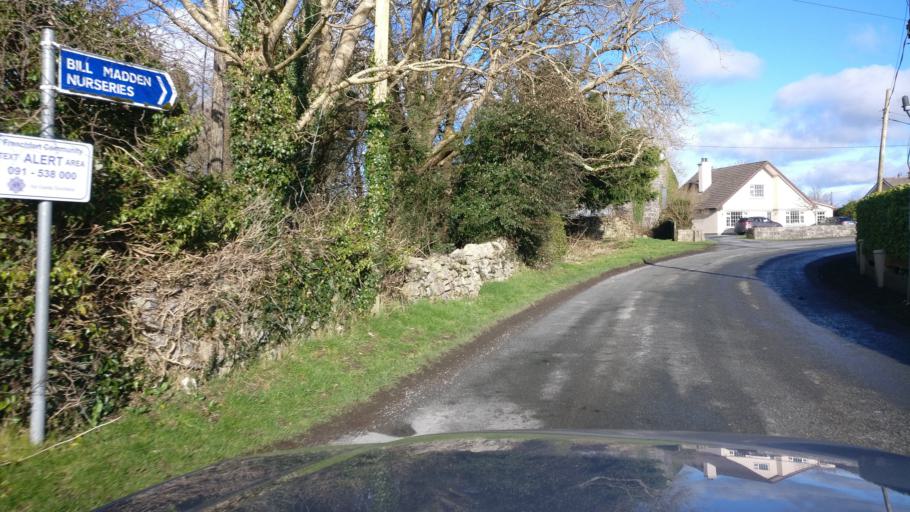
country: IE
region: Connaught
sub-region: County Galway
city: Oranmore
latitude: 53.2790
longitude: -8.9065
